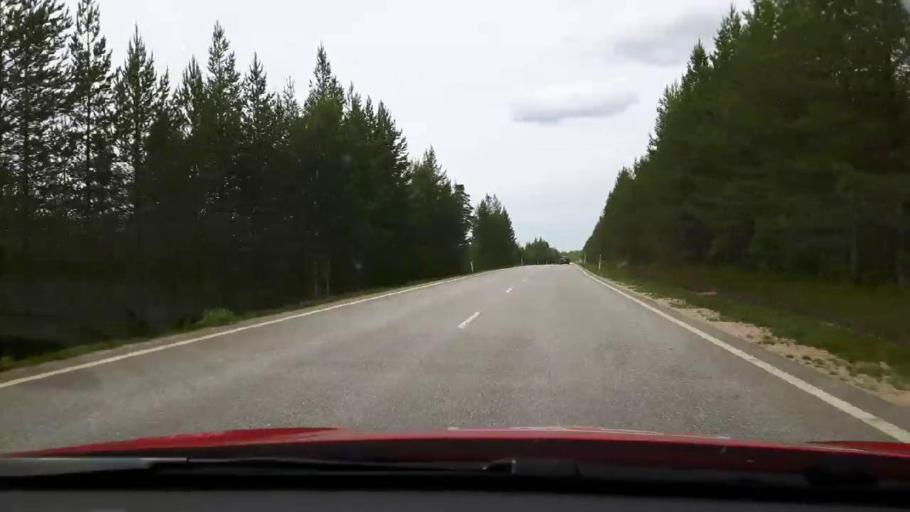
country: SE
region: Jaemtland
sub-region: Harjedalens Kommun
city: Sveg
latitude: 62.0522
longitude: 14.3097
